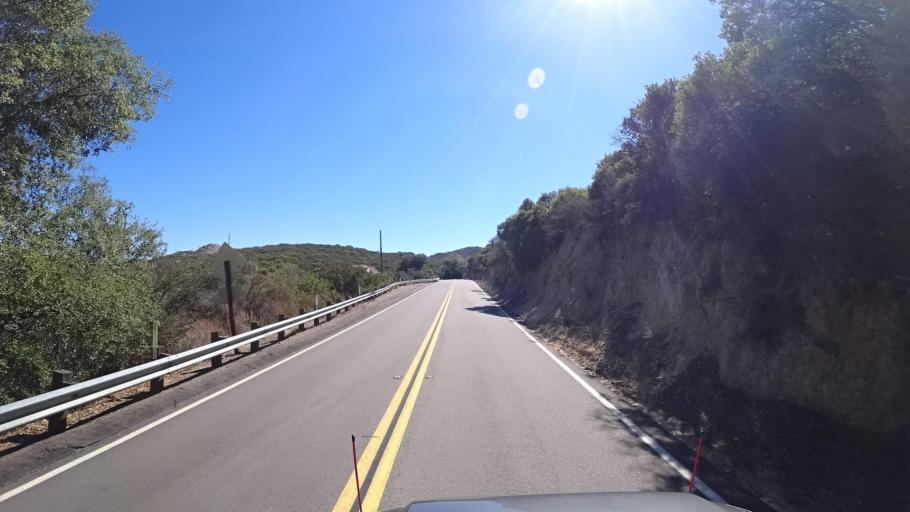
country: US
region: California
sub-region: San Diego County
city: Alpine
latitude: 32.7737
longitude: -116.7076
